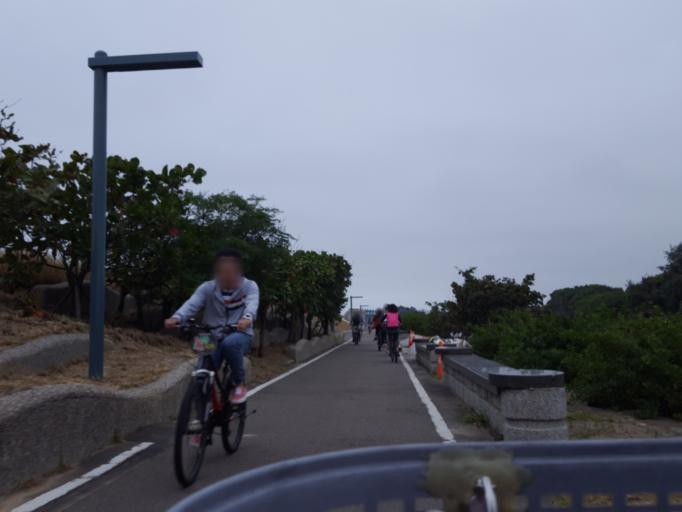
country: TW
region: Taiwan
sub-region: Hsinchu
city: Hsinchu
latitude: 24.8213
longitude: 120.9087
